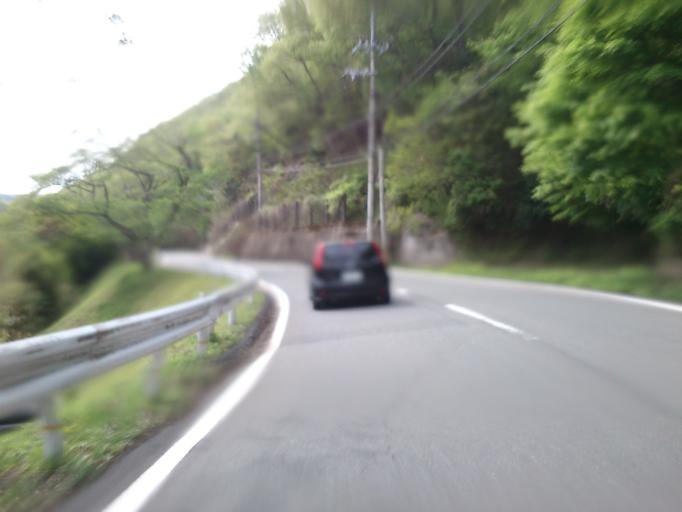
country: JP
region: Kyoto
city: Ayabe
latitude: 35.2692
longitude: 135.4633
